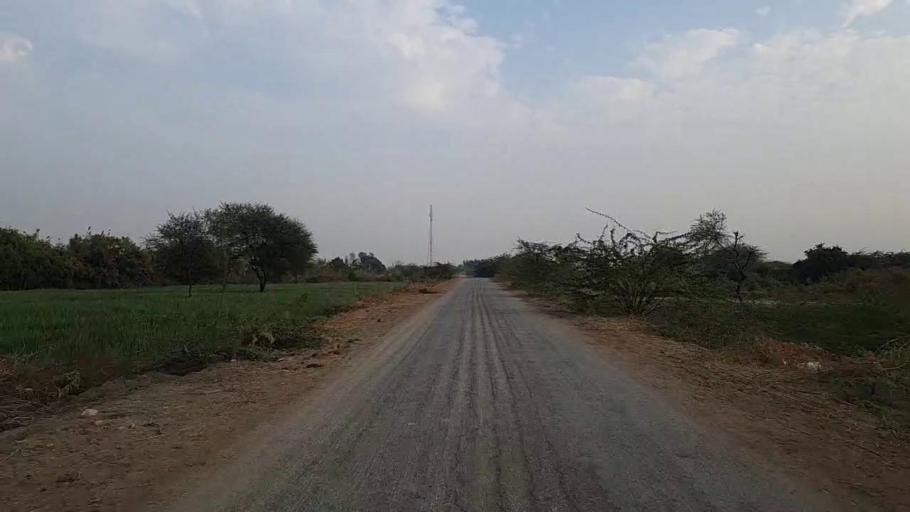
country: PK
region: Sindh
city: Samaro
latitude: 25.3844
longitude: 69.3287
